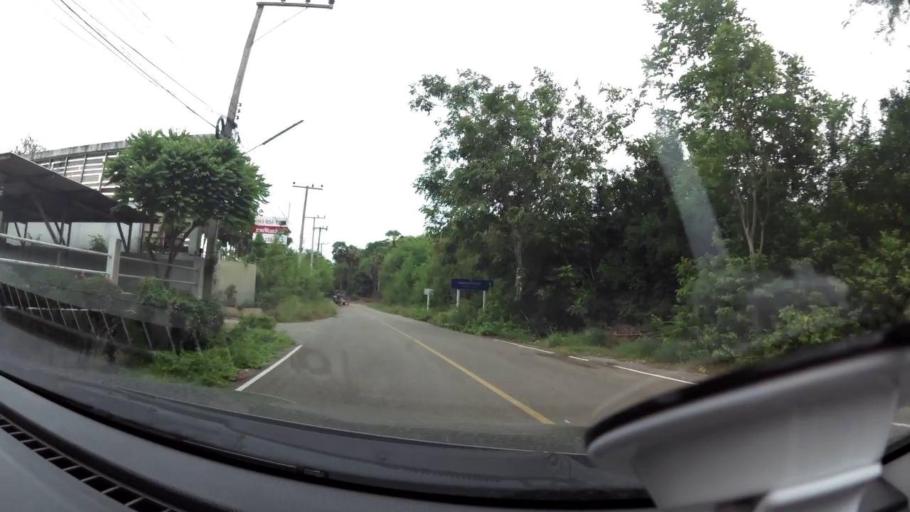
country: TH
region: Prachuap Khiri Khan
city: Pran Buri
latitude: 12.4295
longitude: 99.9784
